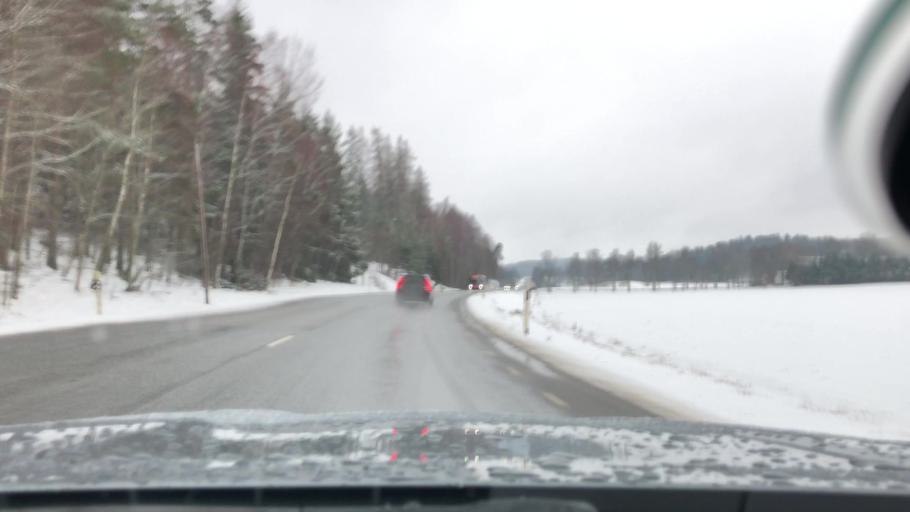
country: SE
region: Stockholm
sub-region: Sodertalje Kommun
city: Pershagen
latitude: 59.0579
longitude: 17.6133
